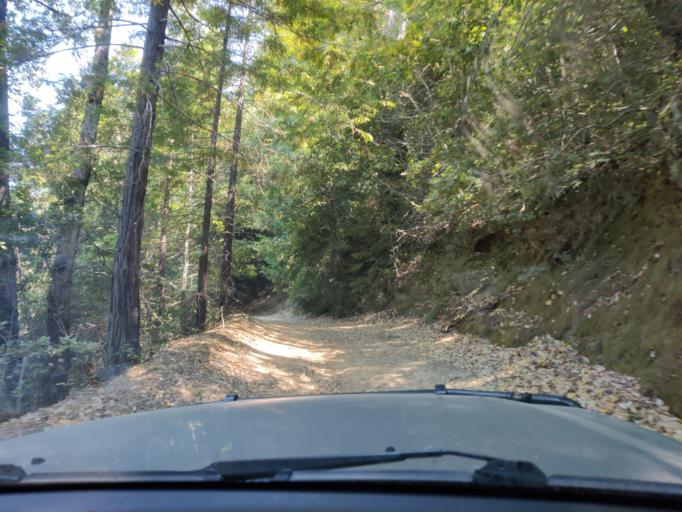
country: US
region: California
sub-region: Humboldt County
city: Redway
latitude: 39.9021
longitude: -123.8885
